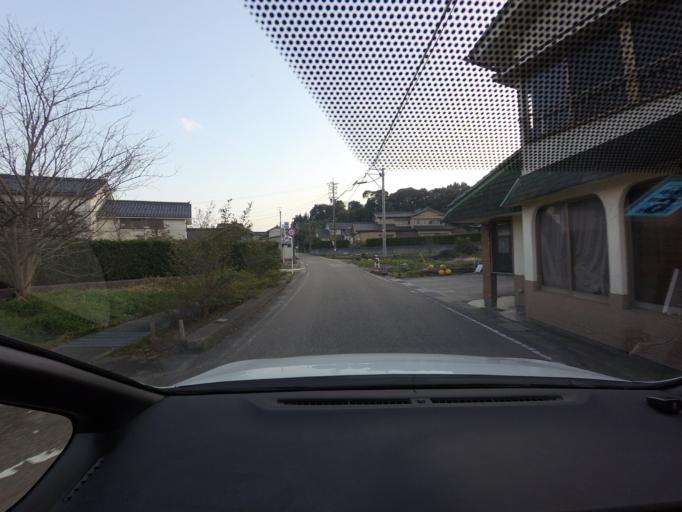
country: JP
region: Ishikawa
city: Nanao
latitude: 37.1555
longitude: 137.0481
